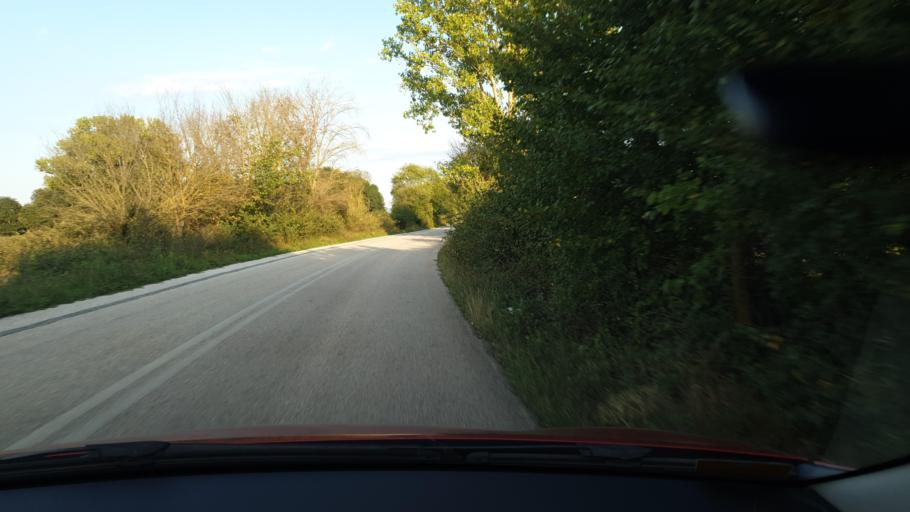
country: GR
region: Central Macedonia
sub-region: Nomos Chalkidikis
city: Galatista
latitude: 40.5643
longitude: 23.3336
